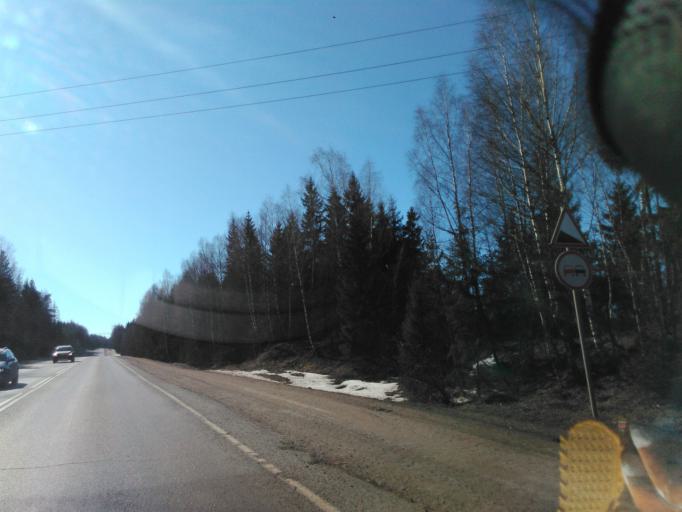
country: RU
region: Moskovskaya
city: Yermolino
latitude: 56.1288
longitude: 37.3532
